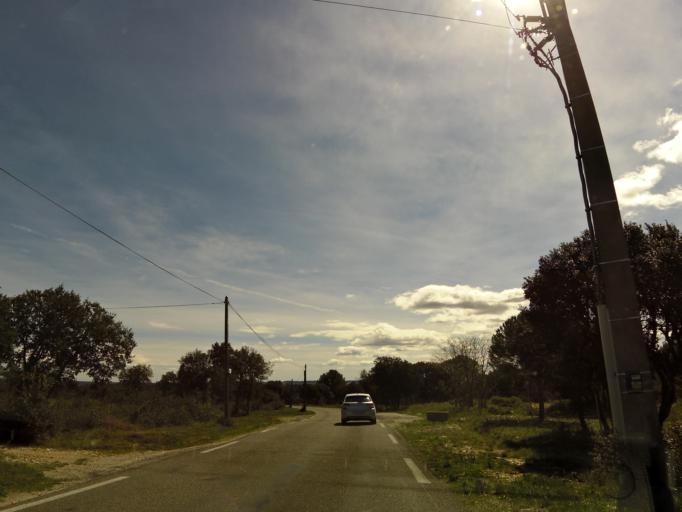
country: FR
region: Languedoc-Roussillon
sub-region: Departement du Gard
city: Langlade
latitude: 43.7894
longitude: 4.2629
